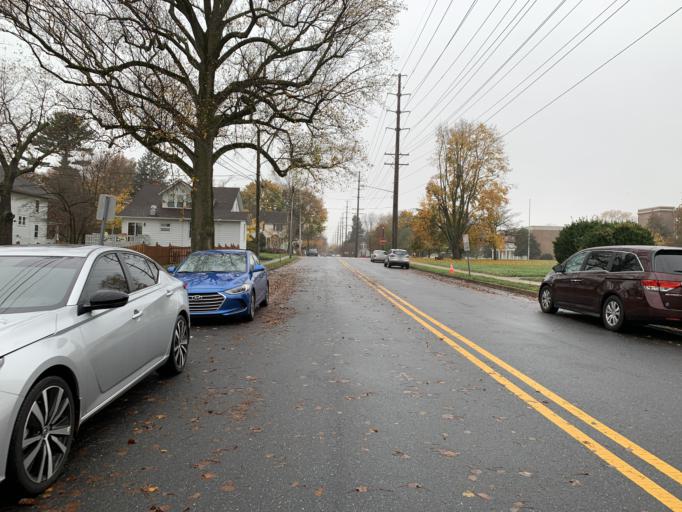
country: US
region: Delaware
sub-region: Kent County
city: Dover
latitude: 39.1639
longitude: -75.5219
